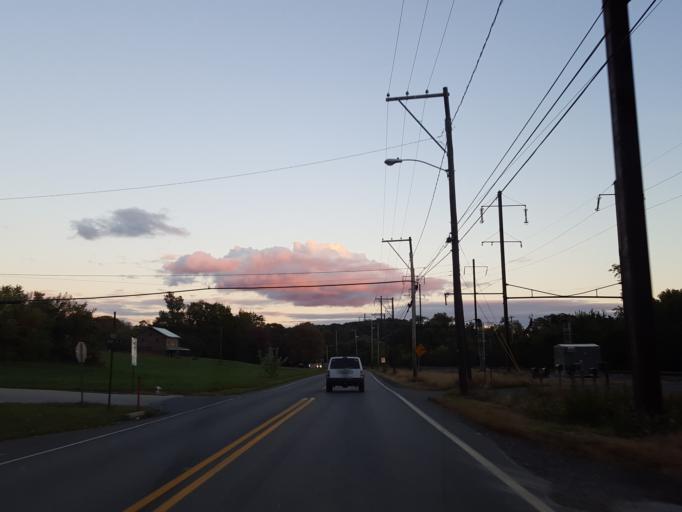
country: US
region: Pennsylvania
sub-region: Lancaster County
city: Columbia
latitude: 40.0282
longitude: -76.5029
